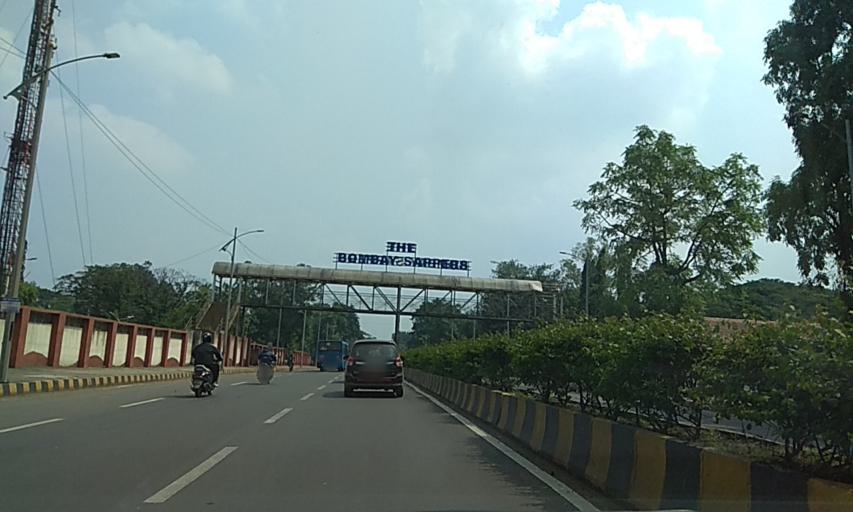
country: IN
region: Maharashtra
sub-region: Pune Division
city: Khadki
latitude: 18.5509
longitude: 73.8678
